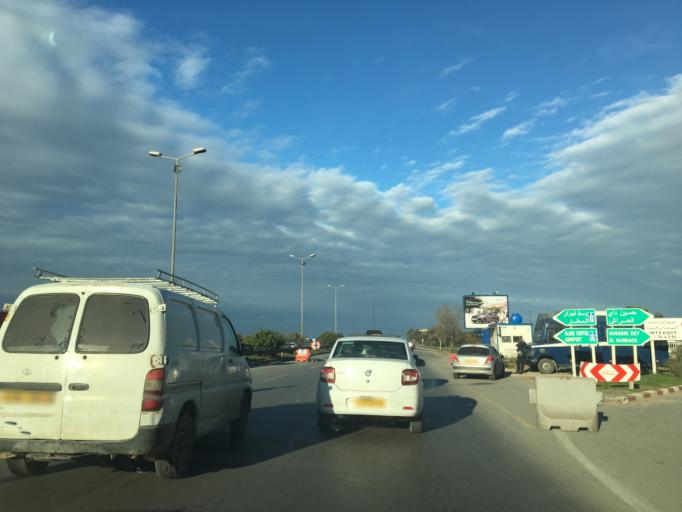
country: DZ
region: Alger
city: Bab Ezzouar
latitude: 36.7328
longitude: 3.1195
